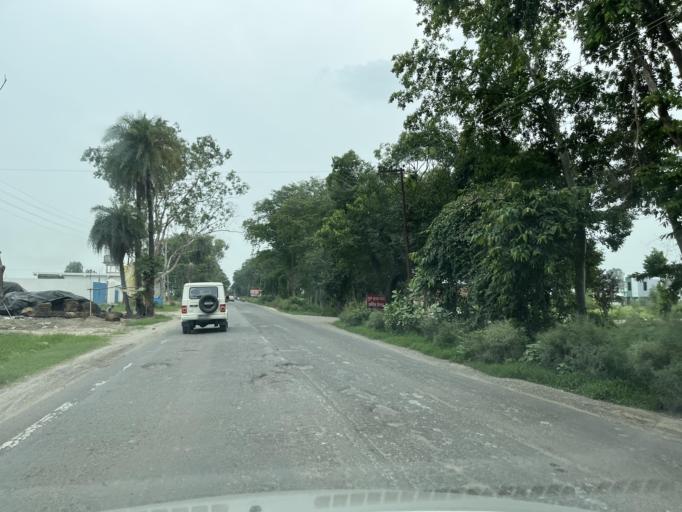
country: IN
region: Uttar Pradesh
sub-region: Rampur
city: Bilaspur
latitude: 29.0291
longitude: 79.2653
